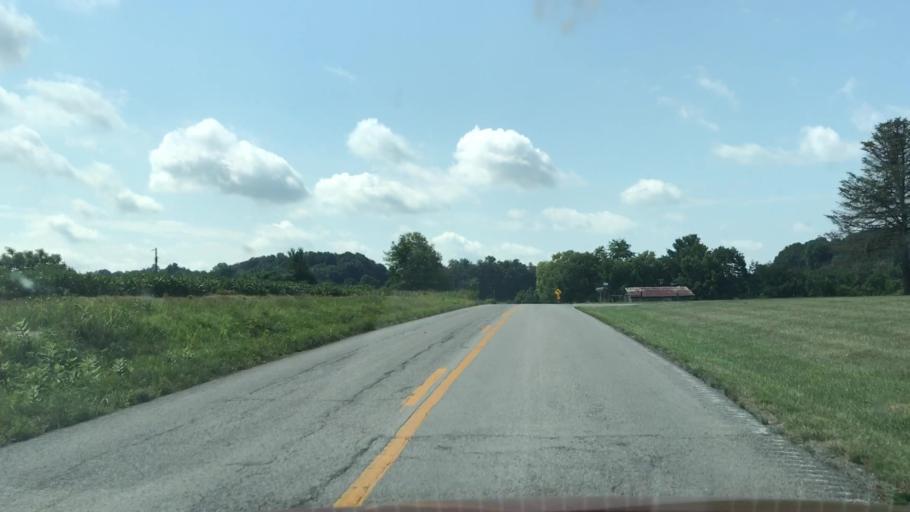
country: US
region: Kentucky
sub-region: Barren County
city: Glasgow
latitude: 36.8461
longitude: -85.8369
